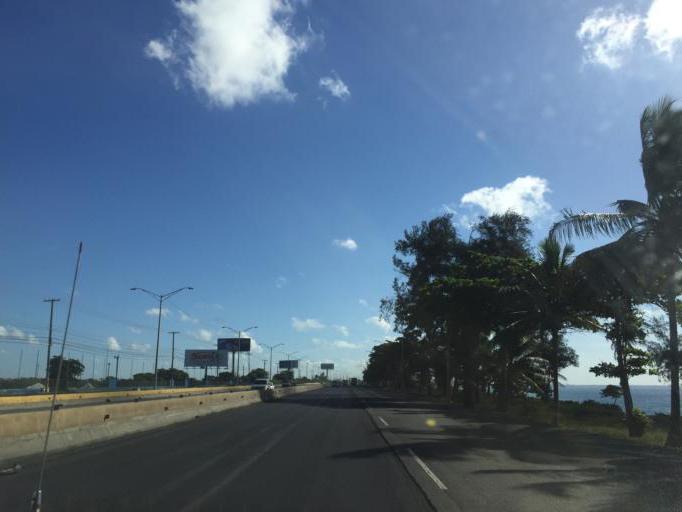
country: DO
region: Santo Domingo
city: Guerra
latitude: 18.4636
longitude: -69.7490
